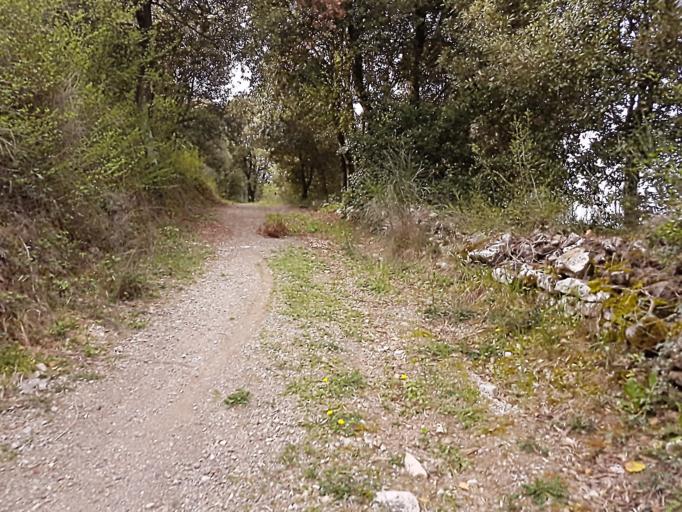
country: IT
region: Umbria
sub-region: Provincia di Perugia
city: Corciano
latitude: 43.1325
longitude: 12.3062
